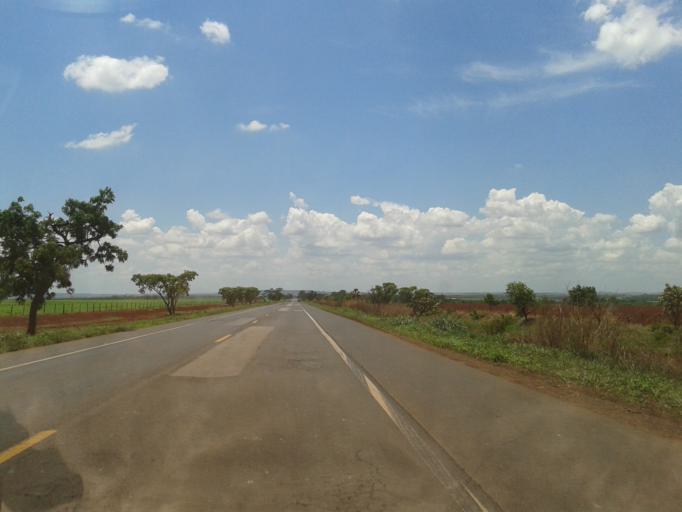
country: BR
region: Goias
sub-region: Goiatuba
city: Goiatuba
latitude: -18.2809
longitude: -49.6221
